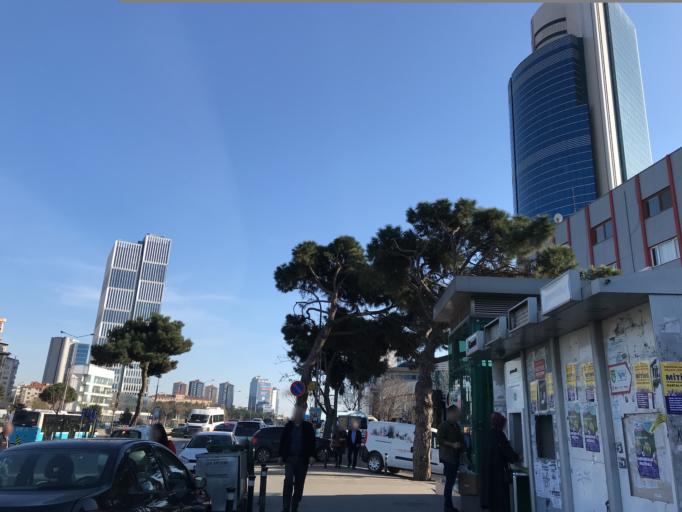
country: TR
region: Istanbul
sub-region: Atasehir
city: Atasehir
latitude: 40.9752
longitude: 29.0986
